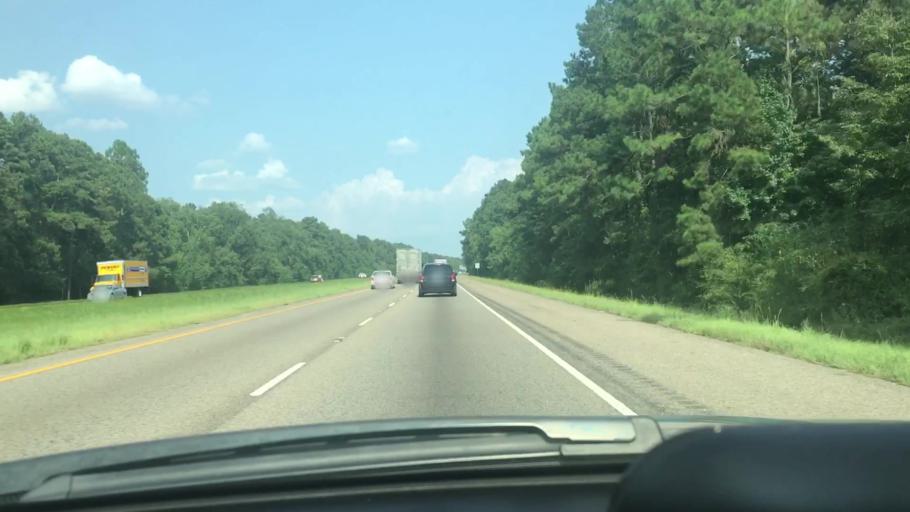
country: US
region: Louisiana
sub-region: Livingston Parish
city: Albany
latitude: 30.4785
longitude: -90.5684
